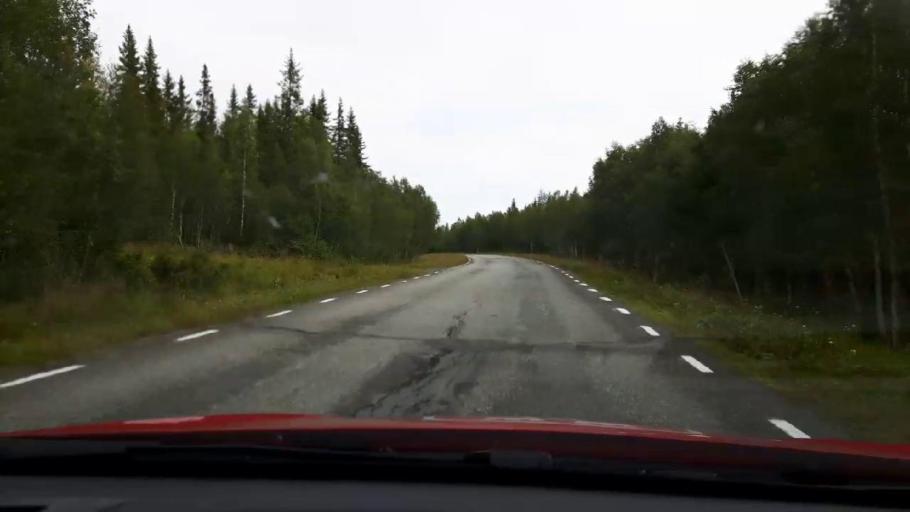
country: SE
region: Jaemtland
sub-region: Are Kommun
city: Are
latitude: 63.7373
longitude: 13.0233
